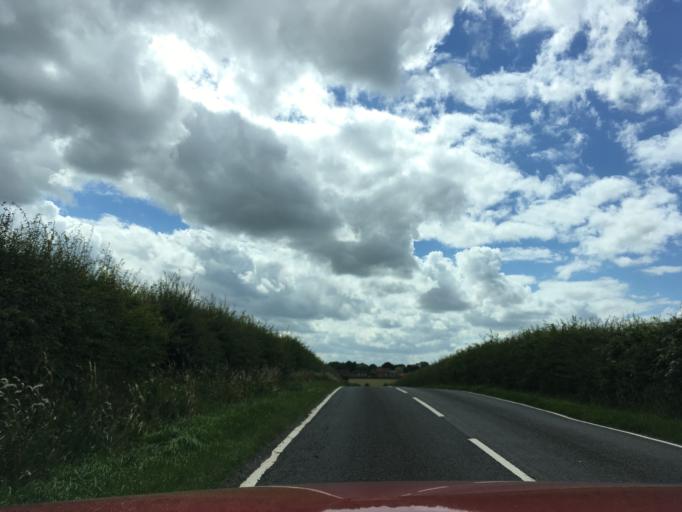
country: GB
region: England
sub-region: Nottinghamshire
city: Ruddington
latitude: 52.8765
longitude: -1.1233
